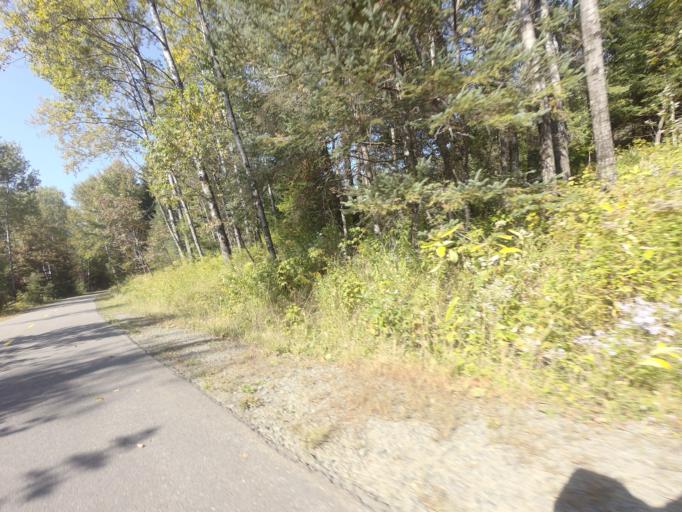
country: CA
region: Quebec
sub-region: Laurentides
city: Mont-Tremblant
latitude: 46.1270
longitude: -74.5718
